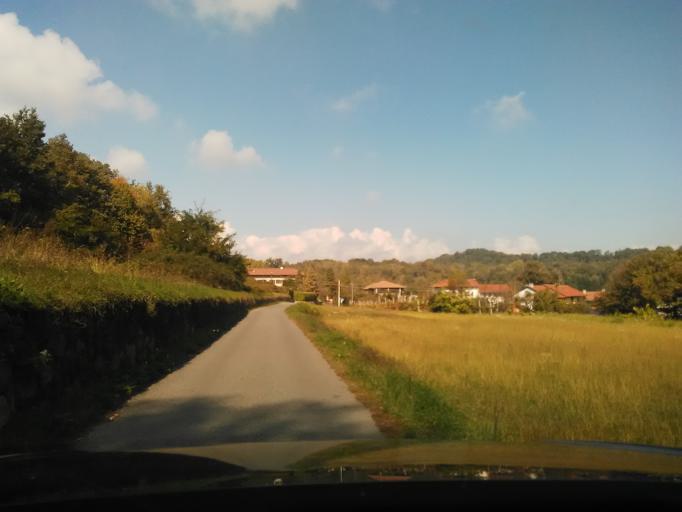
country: IT
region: Piedmont
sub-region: Provincia di Biella
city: Roppolo
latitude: 45.4246
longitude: 8.0812
